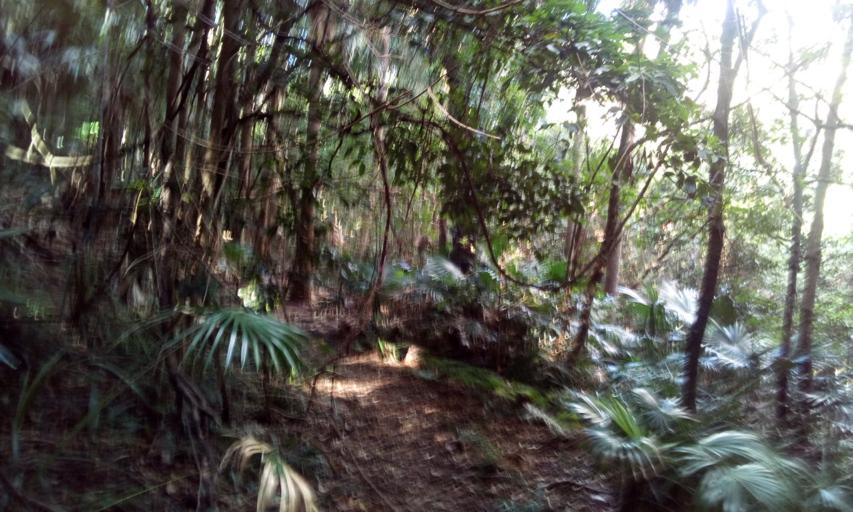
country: AU
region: New South Wales
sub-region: Wollongong
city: Cordeaux Heights
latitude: -34.4436
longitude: 150.7993
